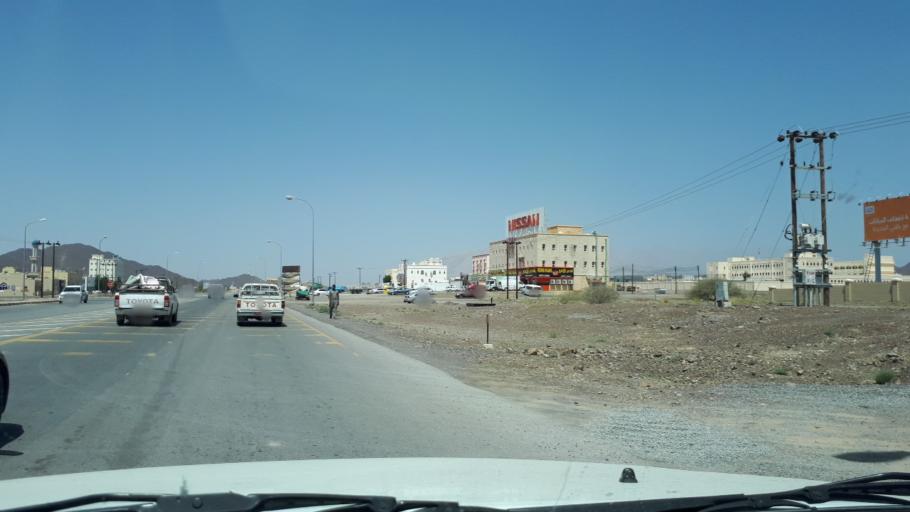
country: OM
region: Muhafazat ad Dakhiliyah
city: Bahla'
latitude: 22.9476
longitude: 57.2611
